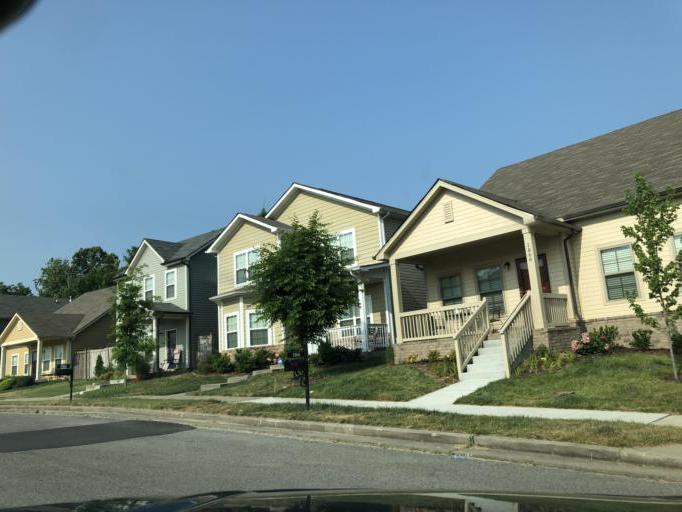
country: US
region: Tennessee
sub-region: Rutherford County
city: La Vergne
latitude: 36.0495
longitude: -86.6430
